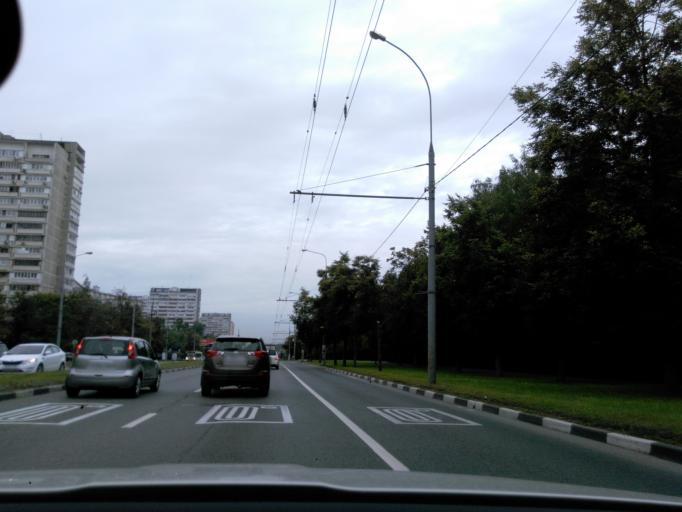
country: RU
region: Moscow
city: Biryulevo
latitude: 55.5941
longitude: 37.6727
